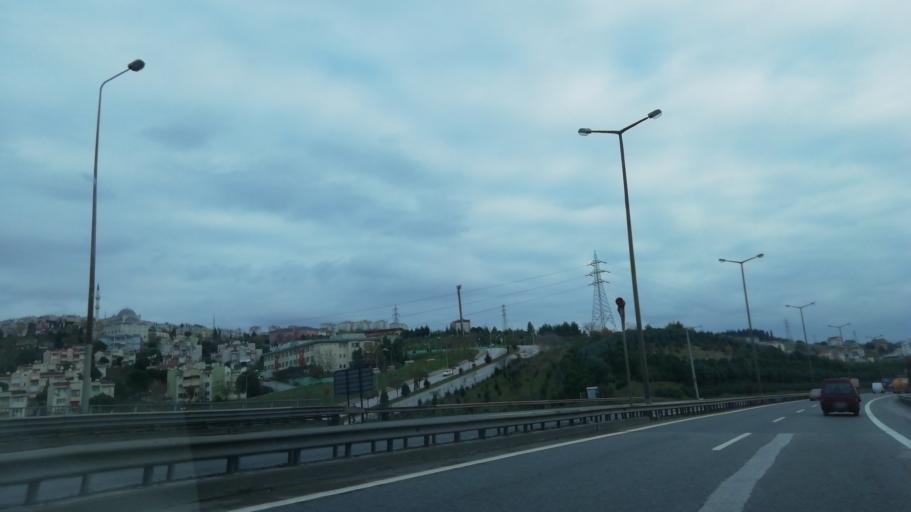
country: TR
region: Kocaeli
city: Izmit
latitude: 40.7847
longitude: 29.9457
